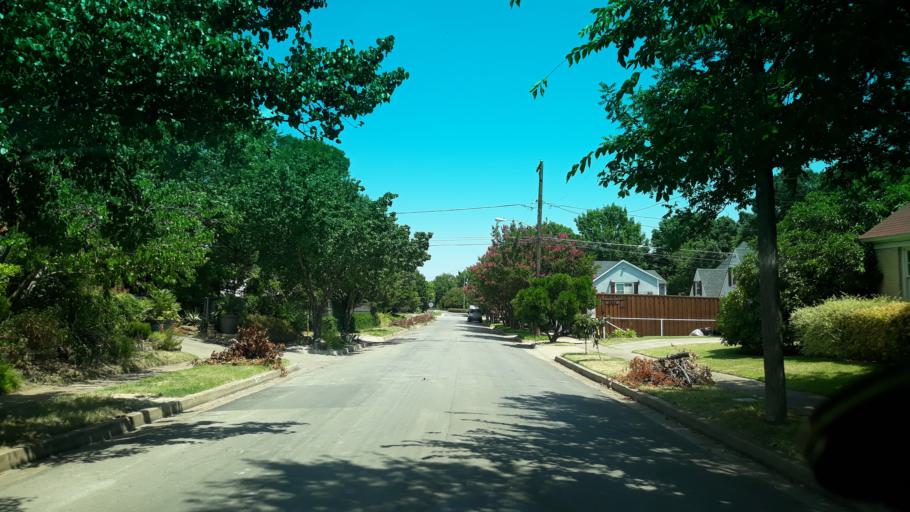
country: US
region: Texas
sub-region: Dallas County
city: Highland Park
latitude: 32.8144
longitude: -96.7404
